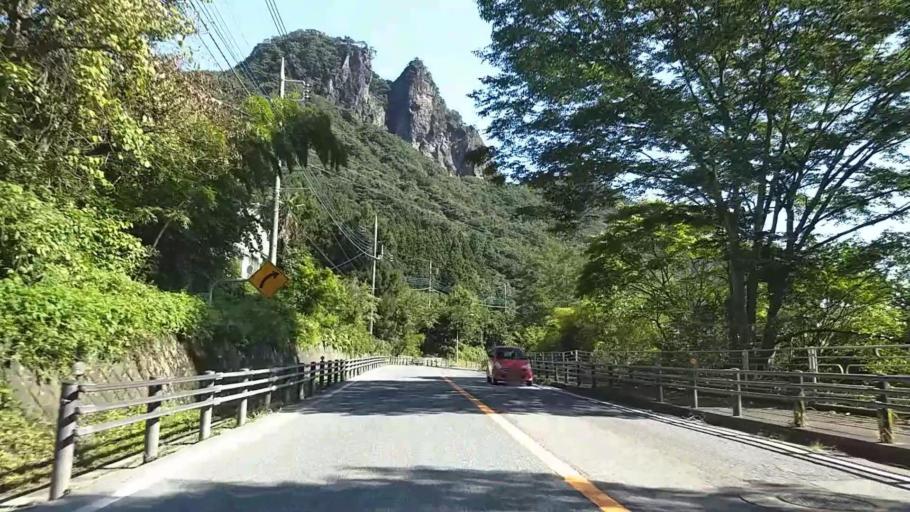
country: JP
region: Gunma
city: Annaka
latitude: 36.3266
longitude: 138.7063
